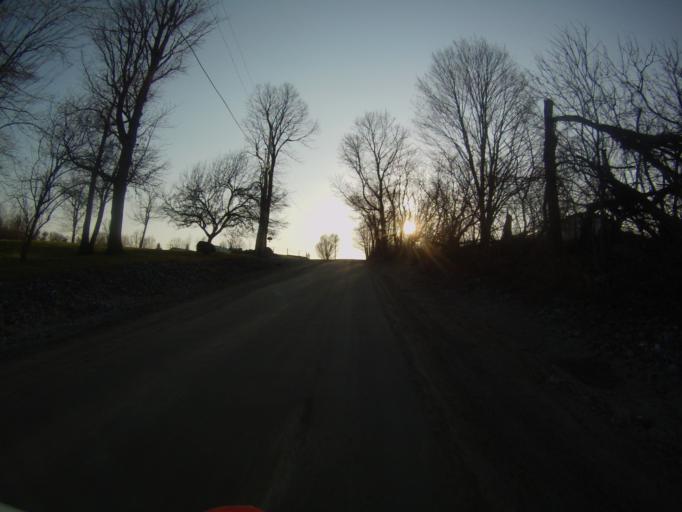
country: US
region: Vermont
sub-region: Addison County
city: Middlebury (village)
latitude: 44.0415
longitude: -73.1156
